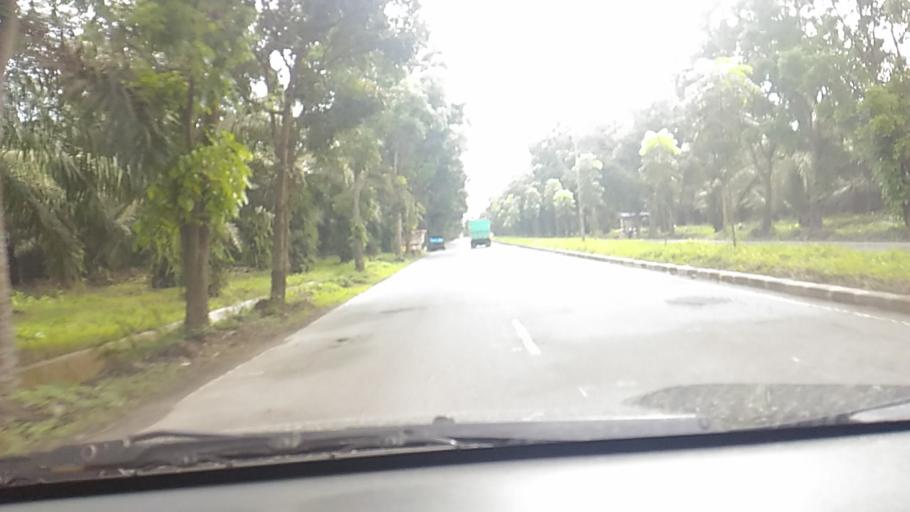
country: ID
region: North Sumatra
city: Binjai
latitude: 3.6508
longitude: 98.5243
